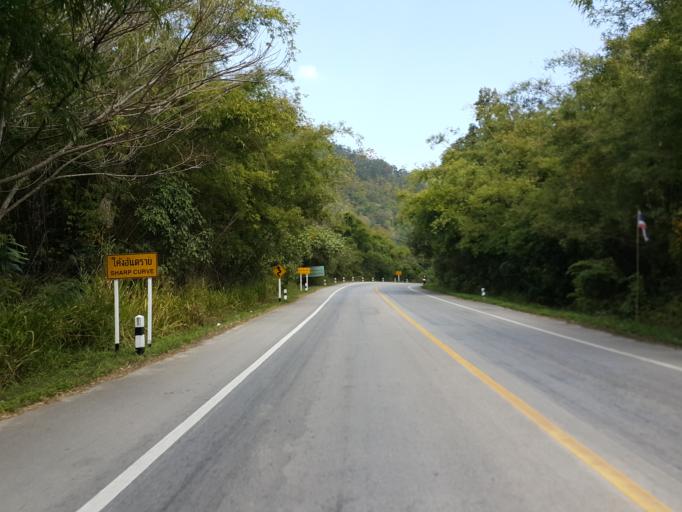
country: TH
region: Lampang
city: Wang Nuea
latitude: 19.0865
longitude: 99.4092
